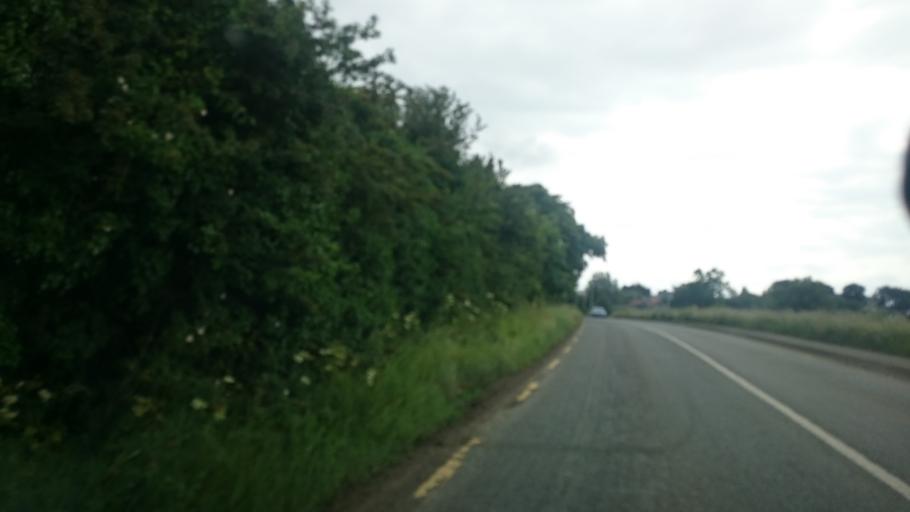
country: IE
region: Leinster
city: Lusk
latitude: 53.5327
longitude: -6.1643
